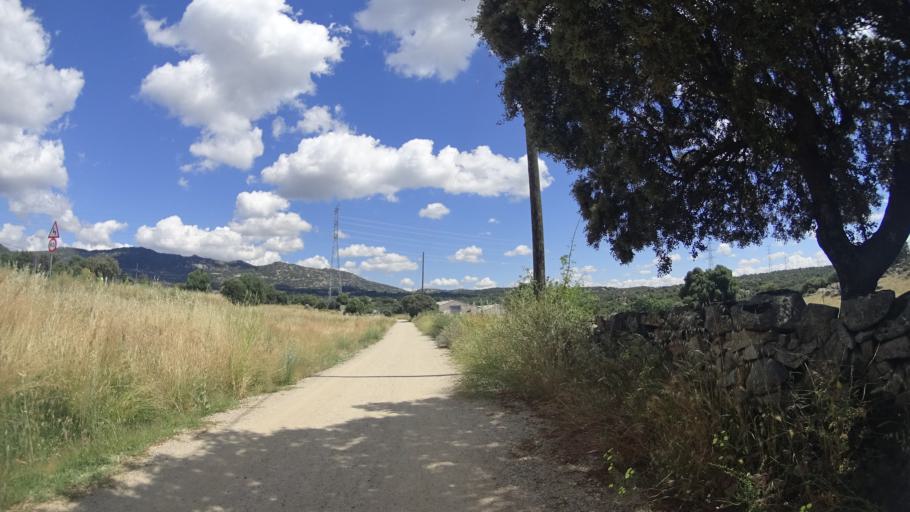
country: ES
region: Madrid
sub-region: Provincia de Madrid
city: Hoyo de Manzanares
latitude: 40.6101
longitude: -3.9035
